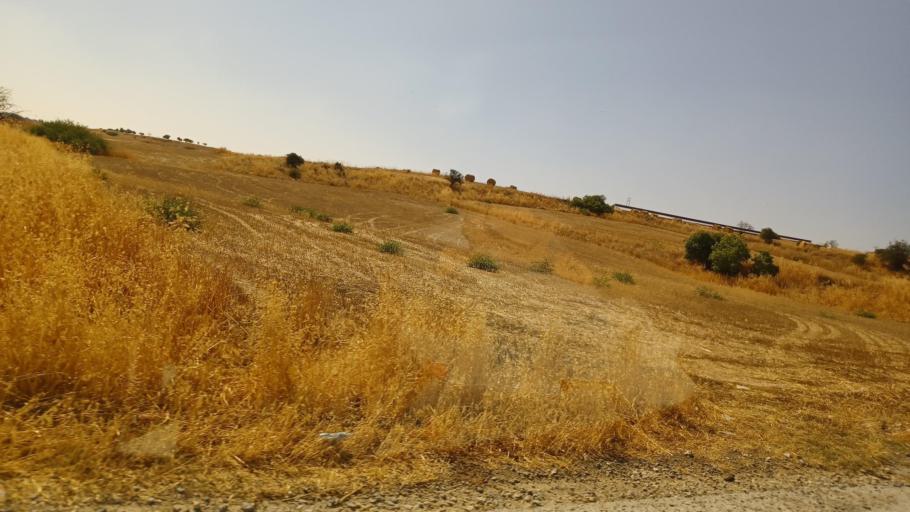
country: CY
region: Larnaka
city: Athienou
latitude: 35.0479
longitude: 33.5368
